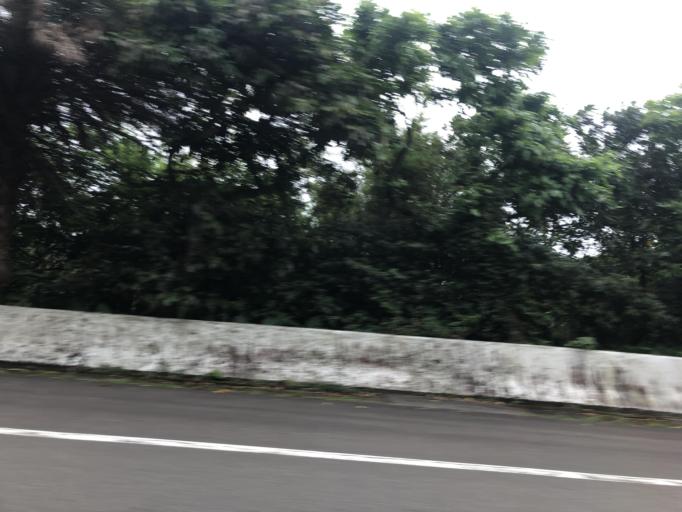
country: TW
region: Taiwan
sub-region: Keelung
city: Keelung
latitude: 25.1979
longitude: 121.6828
